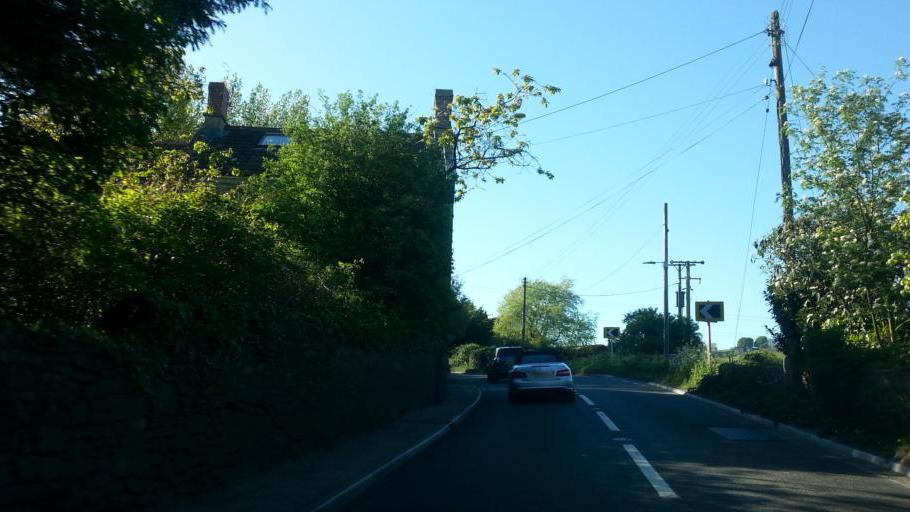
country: GB
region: England
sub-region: Somerset
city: Evercreech
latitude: 51.1624
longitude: -2.5245
